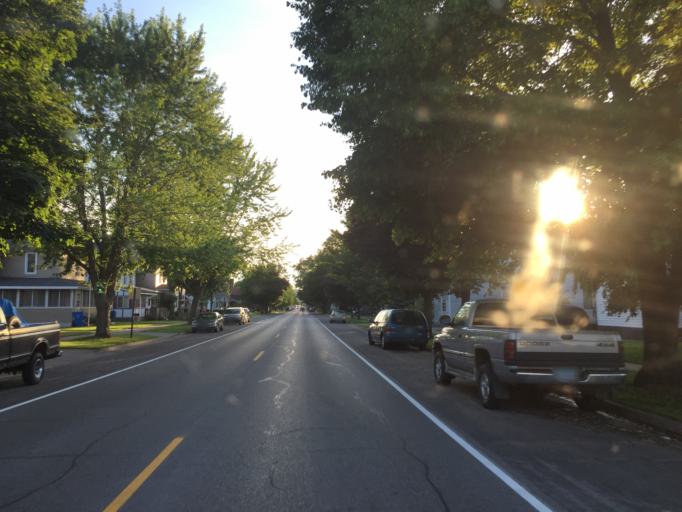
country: US
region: Minnesota
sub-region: Winona County
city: Winona
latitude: 44.0541
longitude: -91.6521
